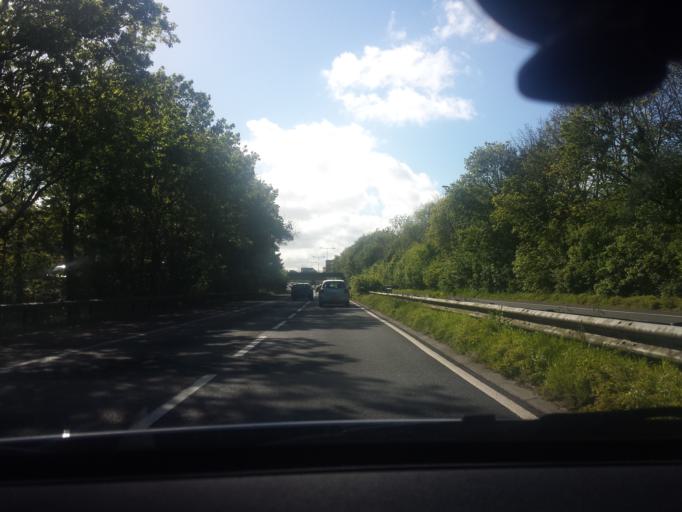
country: GB
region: Wales
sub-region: Cardiff
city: Cardiff
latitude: 51.5040
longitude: -3.1798
